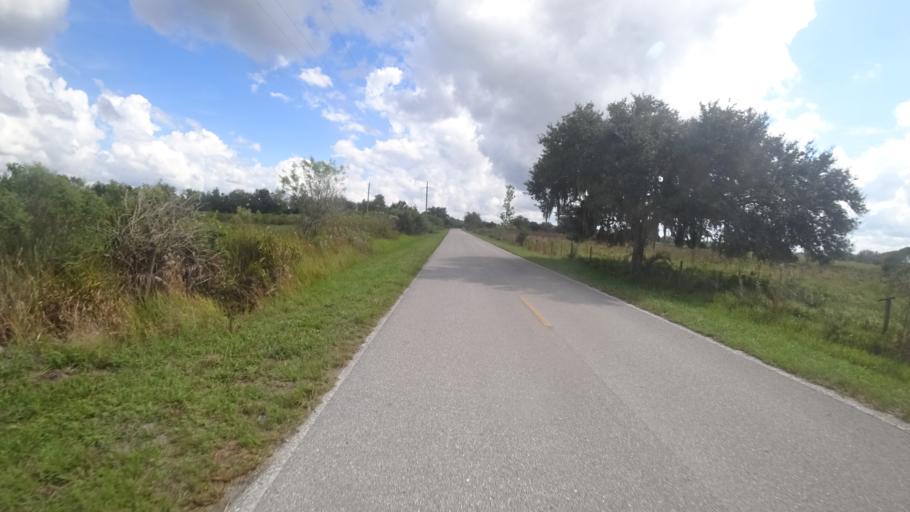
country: US
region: Florida
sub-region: Hillsborough County
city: Wimauma
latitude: 27.6093
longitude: -82.2229
